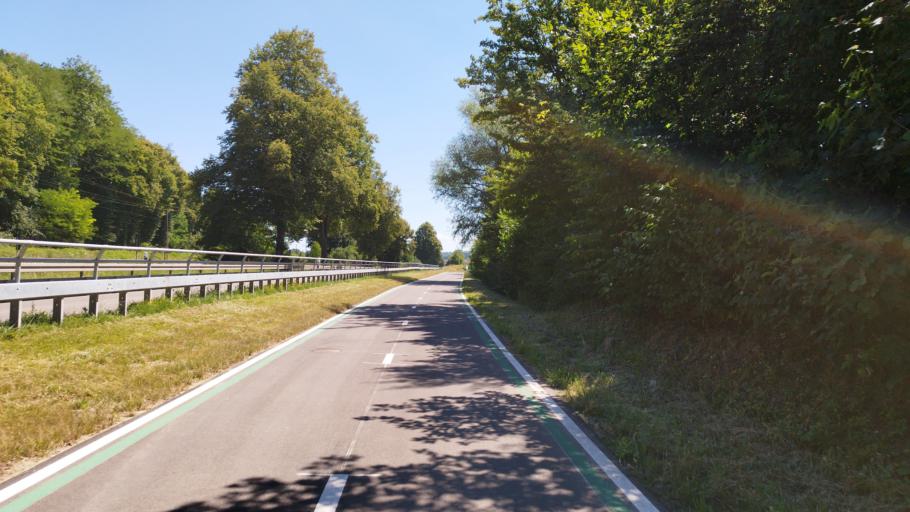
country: DE
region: Baden-Wuerttemberg
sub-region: Regierungsbezirk Stuttgart
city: Ebersbach an der Fils
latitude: 48.7134
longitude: 9.4951
